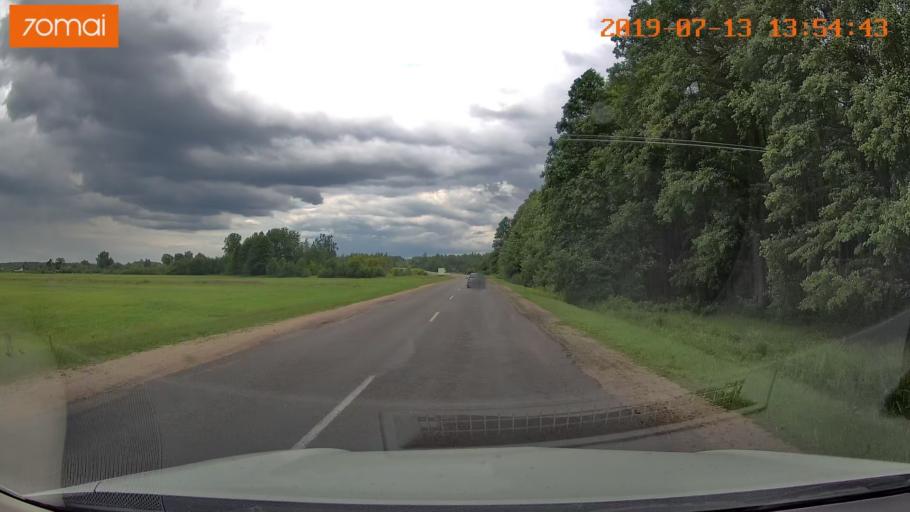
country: BY
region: Mogilev
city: Asipovichy
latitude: 53.2834
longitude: 28.6582
